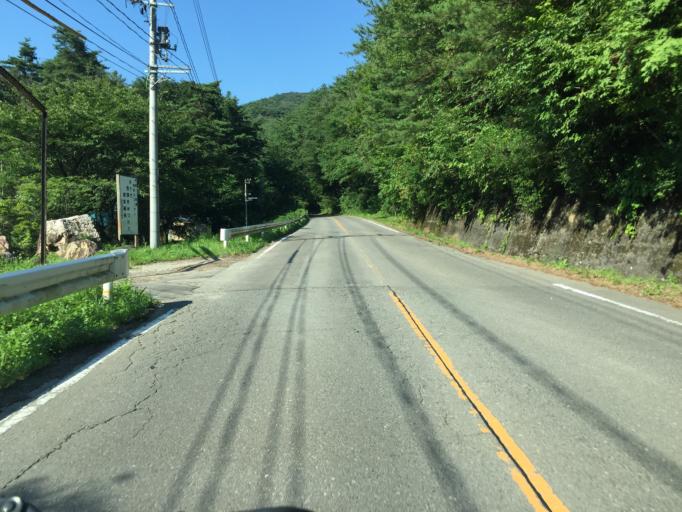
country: JP
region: Fukushima
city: Fukushima-shi
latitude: 37.8507
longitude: 140.4361
